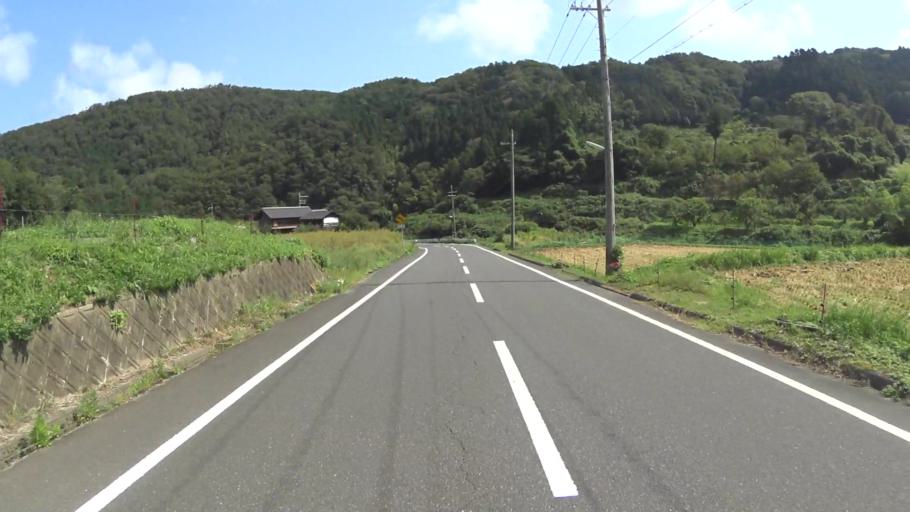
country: JP
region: Kyoto
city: Miyazu
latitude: 35.7051
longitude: 135.2520
